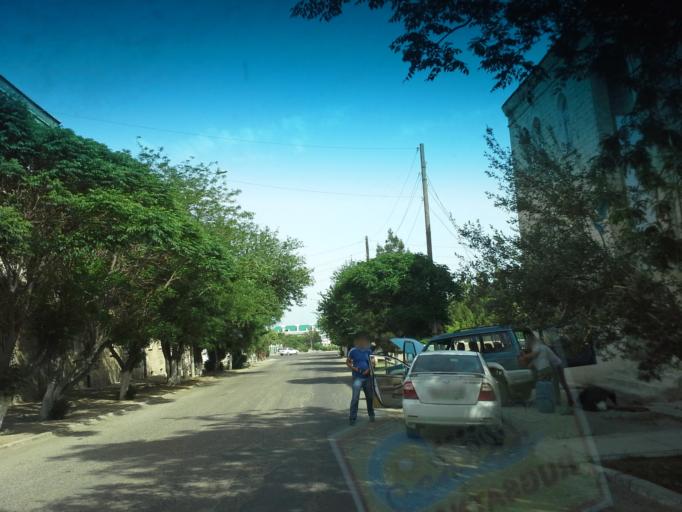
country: TM
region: Balkan
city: Turkmenbasy
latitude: 40.0020
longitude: 52.9912
